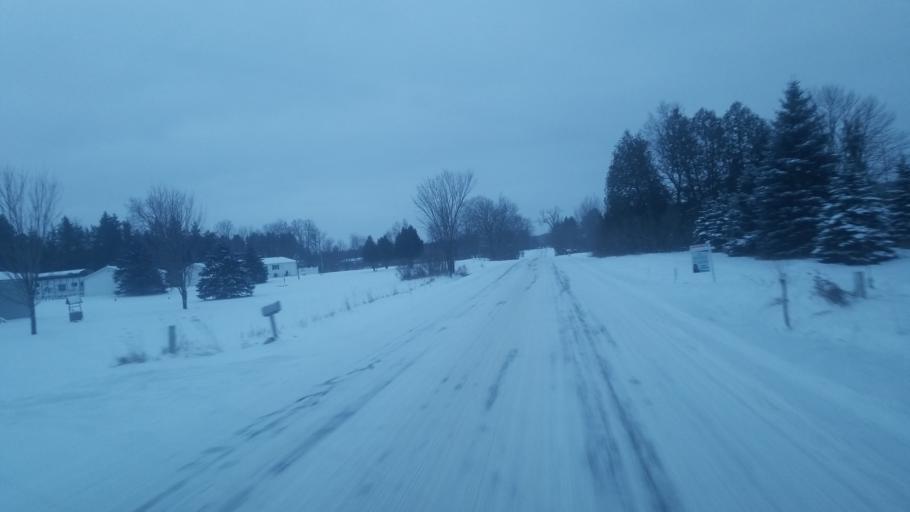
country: US
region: Michigan
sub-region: Osceola County
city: Reed City
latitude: 43.8352
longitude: -85.4242
